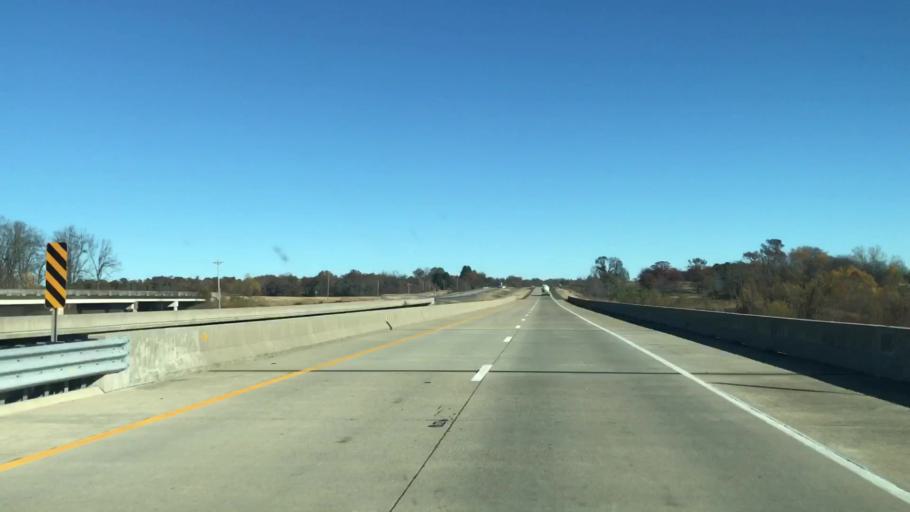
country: US
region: Texas
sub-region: Cass County
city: Queen City
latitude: 33.1482
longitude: -93.8912
